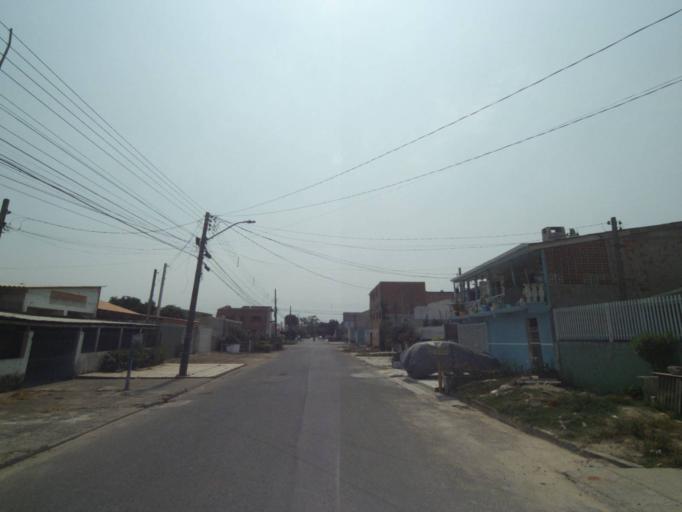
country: BR
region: Parana
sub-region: Pinhais
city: Pinhais
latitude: -25.4849
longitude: -49.1941
